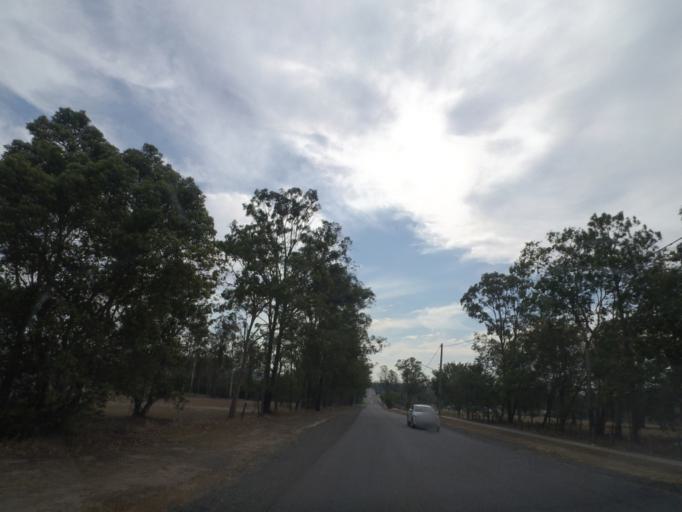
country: AU
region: Queensland
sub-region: Brisbane
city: Richlands
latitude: -27.5929
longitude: 152.9546
